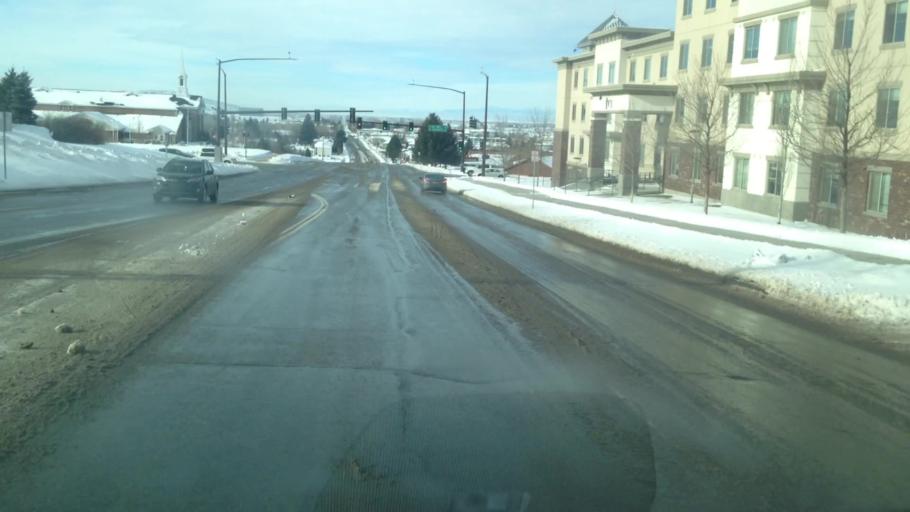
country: US
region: Idaho
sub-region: Madison County
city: Rexburg
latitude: 43.8116
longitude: -111.7879
